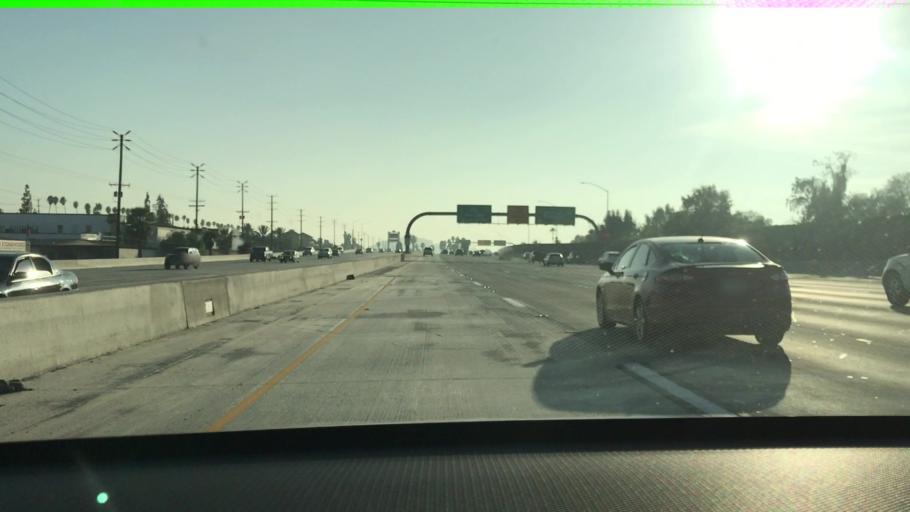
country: US
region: California
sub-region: Riverside County
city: Rubidoux
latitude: 33.9865
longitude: -117.3643
